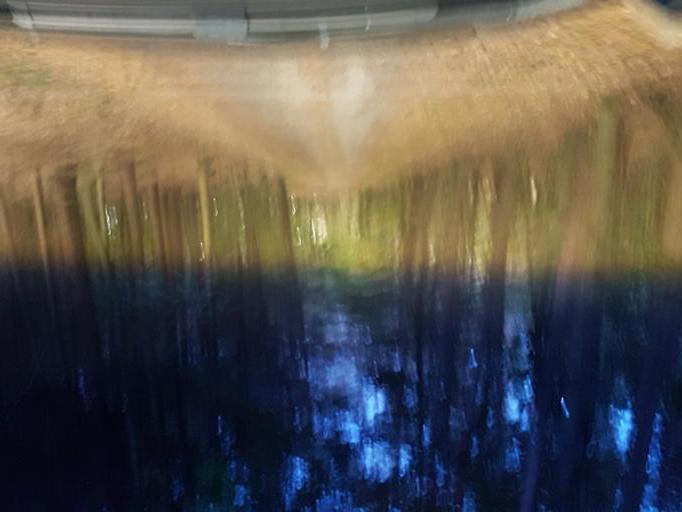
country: DE
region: Bavaria
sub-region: Regierungsbezirk Mittelfranken
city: Markt Taschendorf
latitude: 49.7598
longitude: 10.5403
